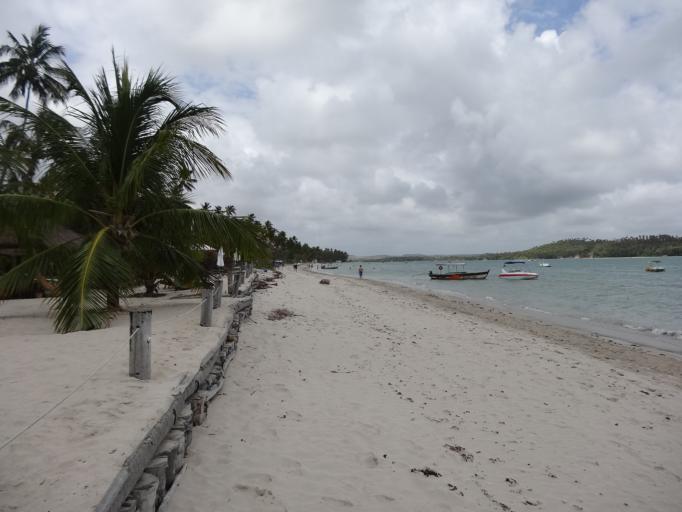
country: BR
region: Pernambuco
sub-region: Tamandare
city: Tamandare
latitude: -8.6995
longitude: -35.0848
